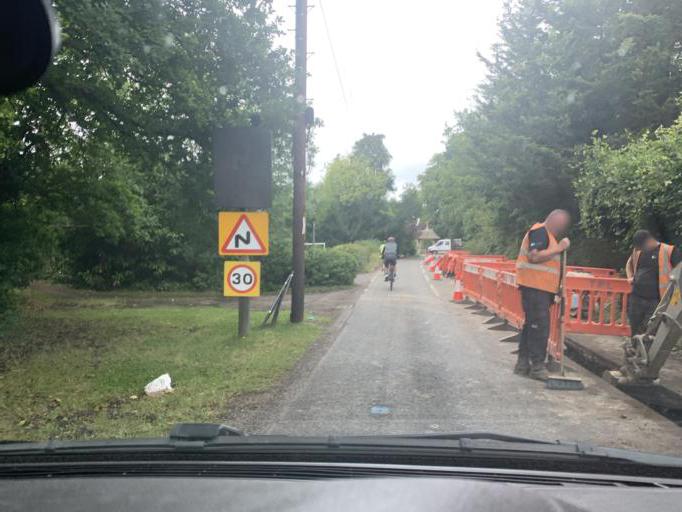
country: GB
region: England
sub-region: Gloucestershire
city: Churchdown
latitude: 51.9006
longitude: -2.1916
